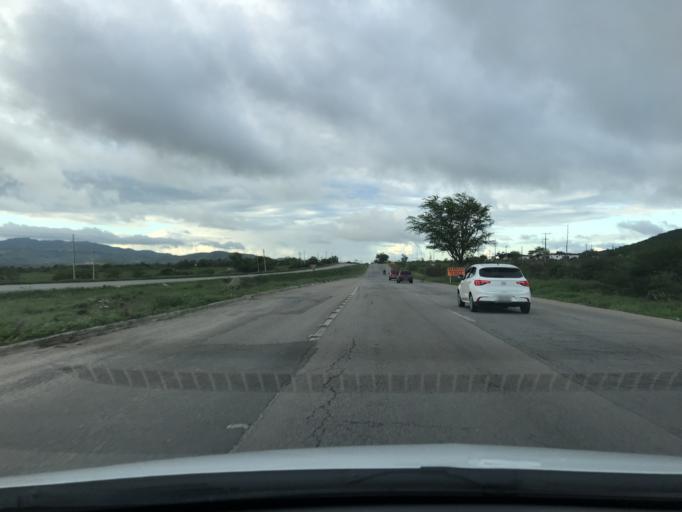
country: BR
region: Pernambuco
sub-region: Bezerros
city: Bezerros
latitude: -8.2880
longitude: -35.8192
